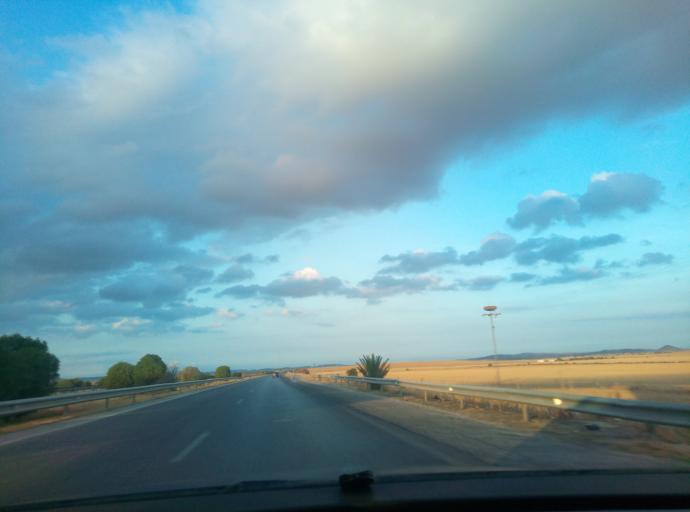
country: TN
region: Manouba
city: El Battan
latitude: 36.6978
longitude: 9.9426
